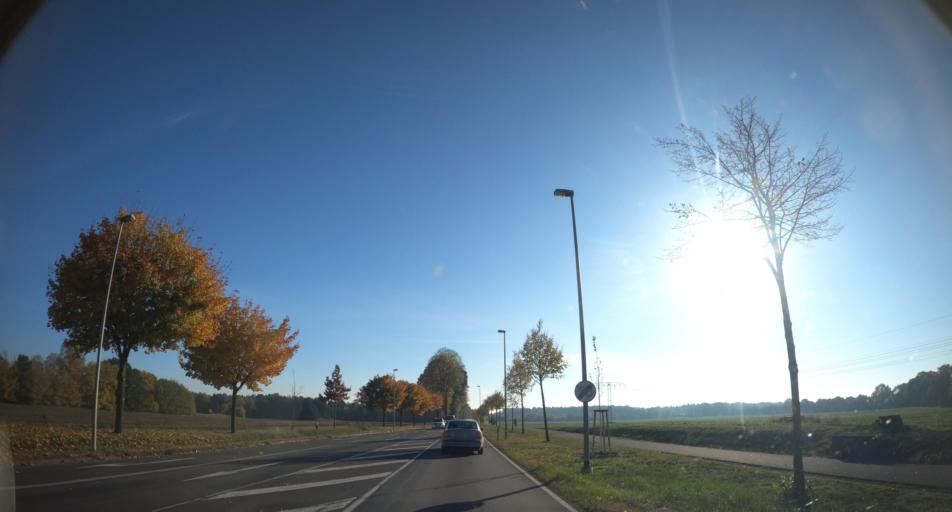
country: DE
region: Mecklenburg-Vorpommern
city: Ueckermunde
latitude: 53.7210
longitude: 14.0628
